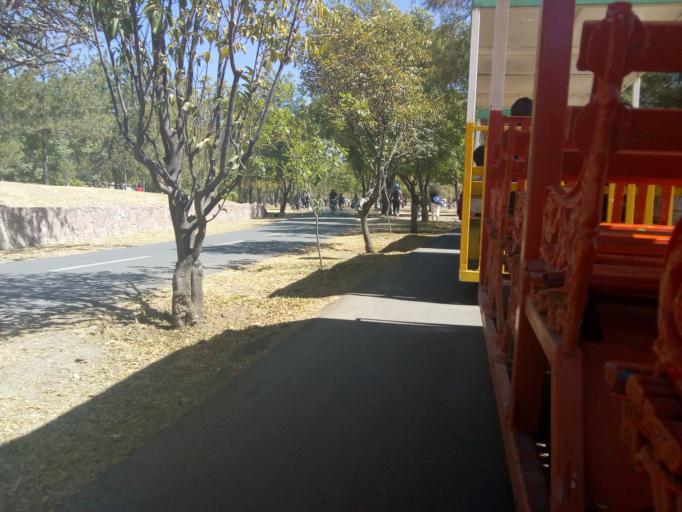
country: MX
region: Guanajuato
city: Leon
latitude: 21.1864
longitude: -101.6793
